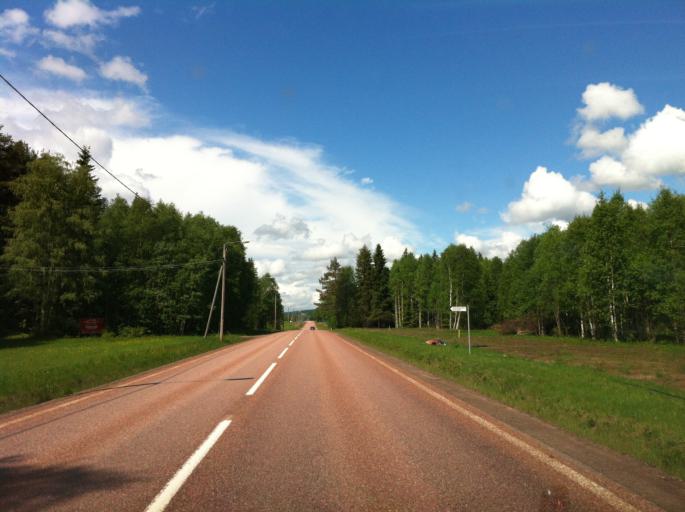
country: SE
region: Dalarna
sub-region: Malung-Saelens kommun
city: Malung
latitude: 61.0597
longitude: 13.3343
